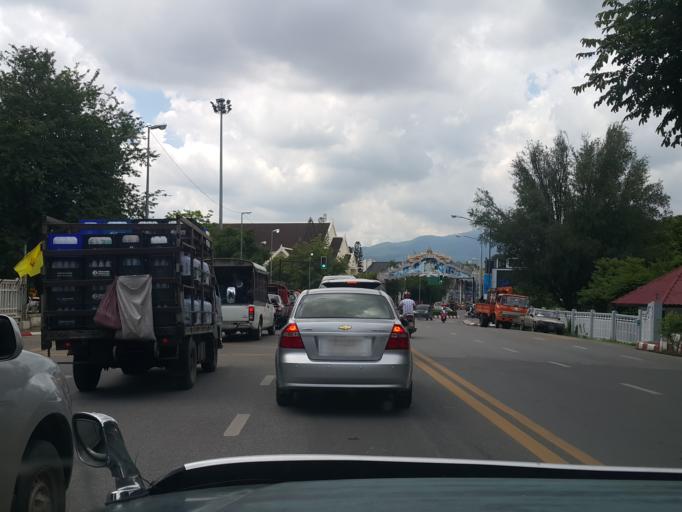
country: TH
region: Chiang Mai
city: Chiang Mai
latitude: 18.7875
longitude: 99.0035
